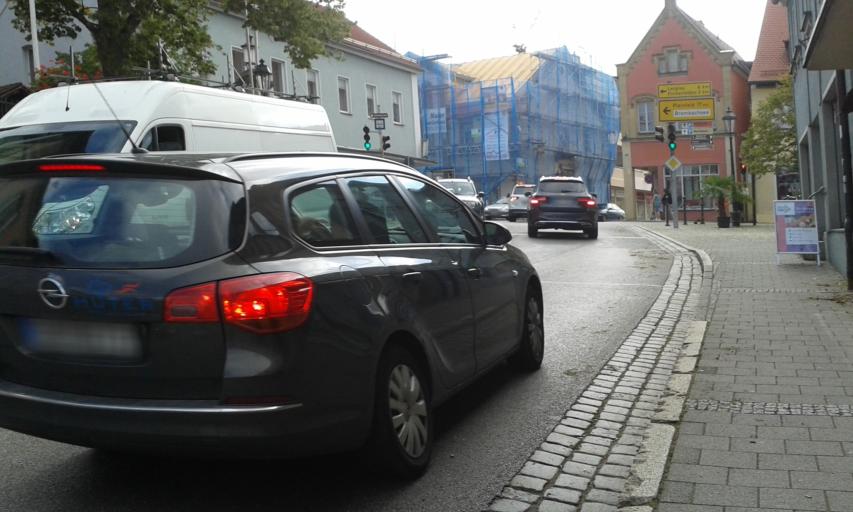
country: DE
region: Bavaria
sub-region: Regierungsbezirk Mittelfranken
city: Gunzenhausen
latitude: 49.1158
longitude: 10.7550
